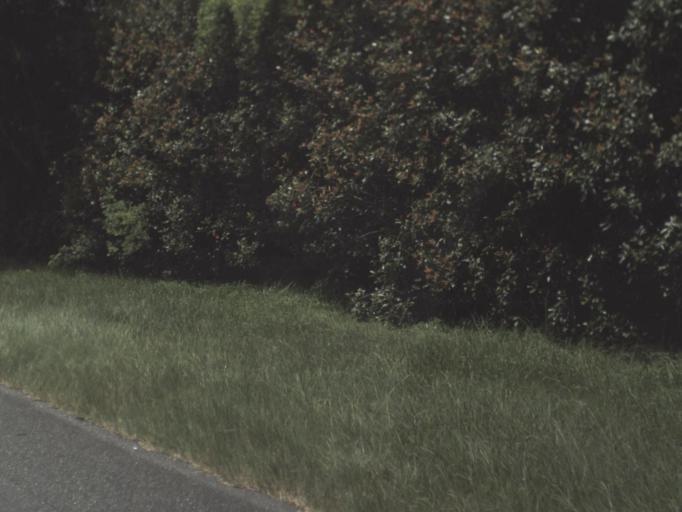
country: US
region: Florida
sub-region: Alachua County
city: Newberry
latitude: 29.6175
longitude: -82.5955
